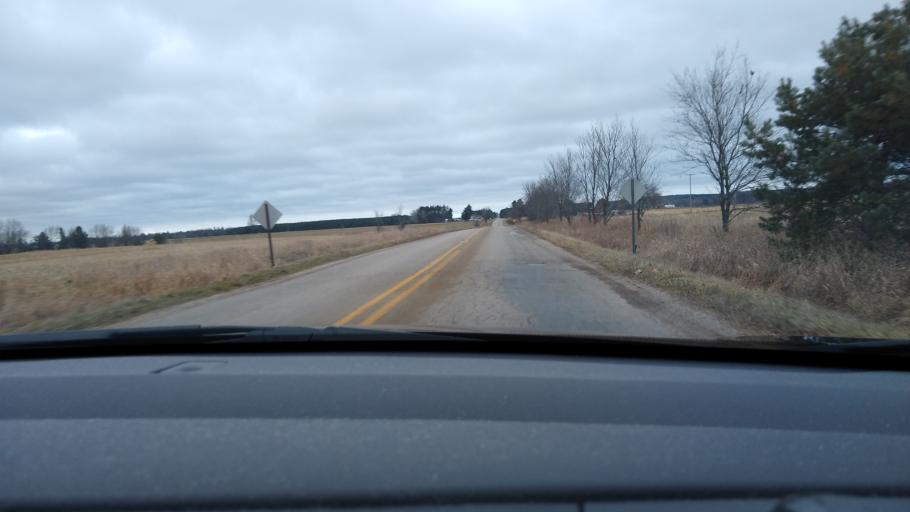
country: US
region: Michigan
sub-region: Missaukee County
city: Lake City
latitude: 44.2451
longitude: -85.0535
